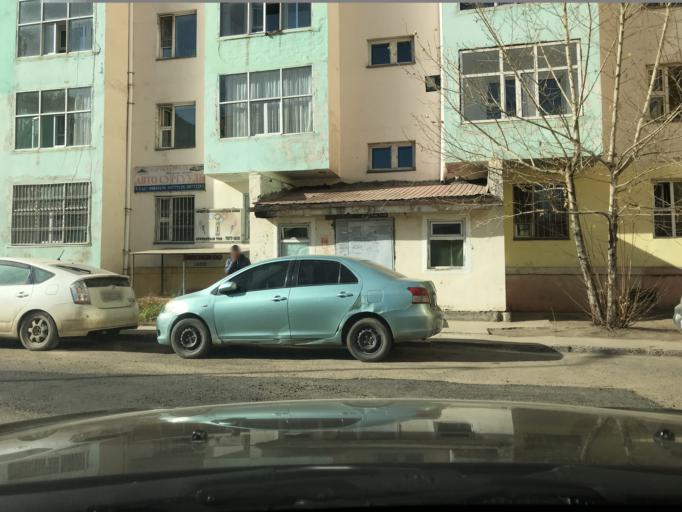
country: MN
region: Ulaanbaatar
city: Ulaanbaatar
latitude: 47.9112
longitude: 106.9406
